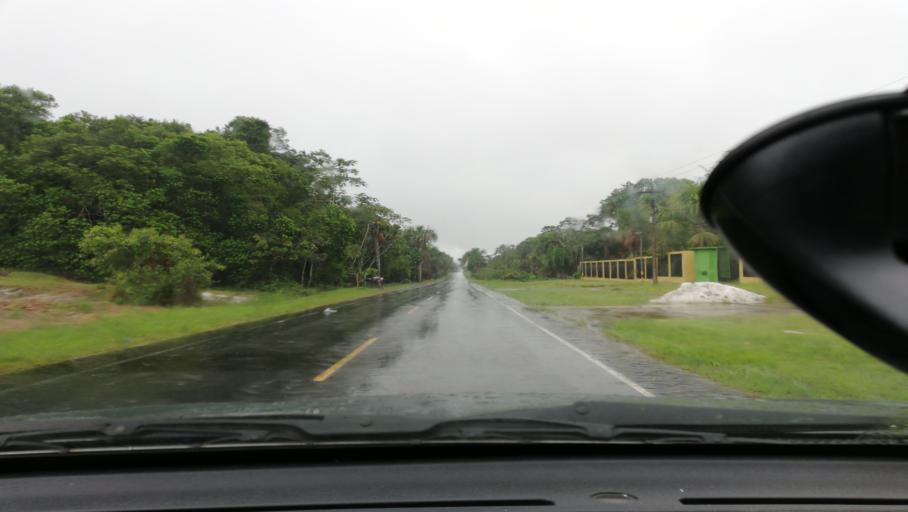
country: PE
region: Loreto
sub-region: Provincia de Maynas
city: San Juan
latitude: -3.9520
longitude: -73.4054
